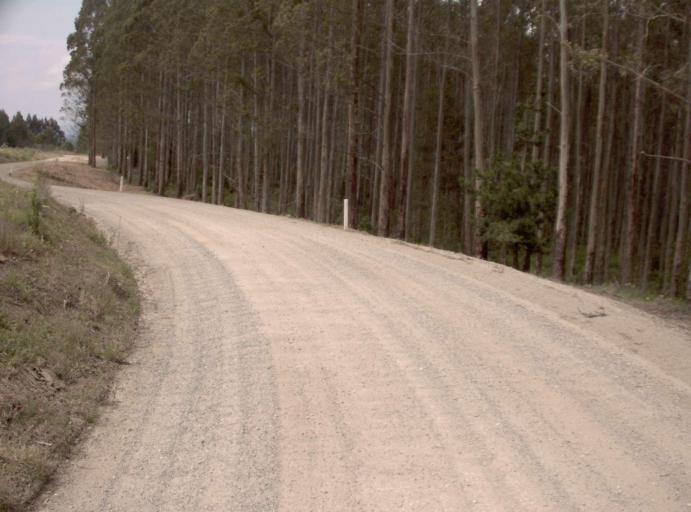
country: AU
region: Victoria
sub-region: Latrobe
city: Traralgon
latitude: -38.3752
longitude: 146.6794
